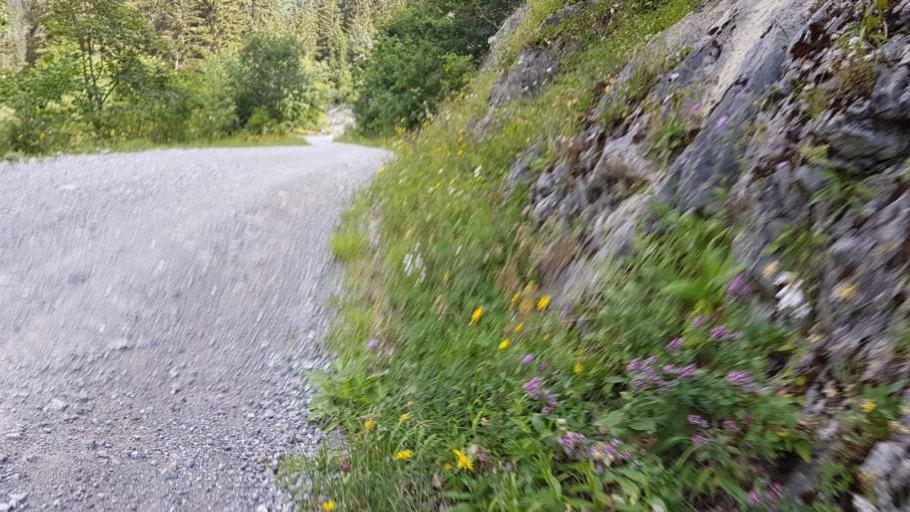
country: CH
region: Bern
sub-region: Obersimmental-Saanen District
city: Boltigen
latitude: 46.6822
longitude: 7.4507
